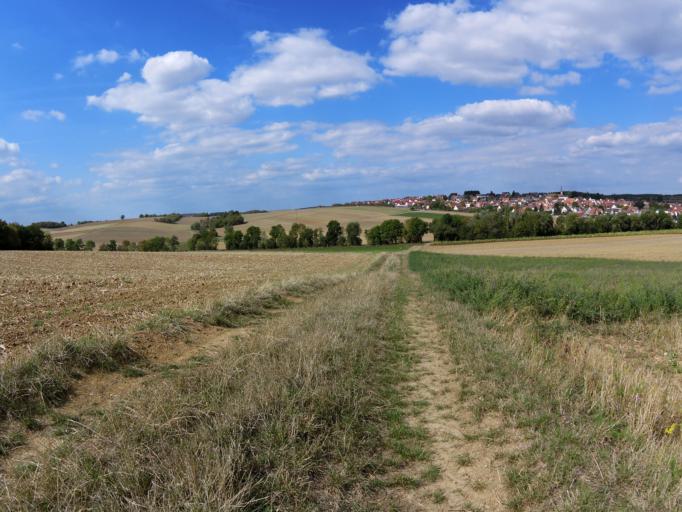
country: DE
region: Bavaria
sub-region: Regierungsbezirk Unterfranken
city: Hettstadt
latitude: 49.7937
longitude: 9.8184
